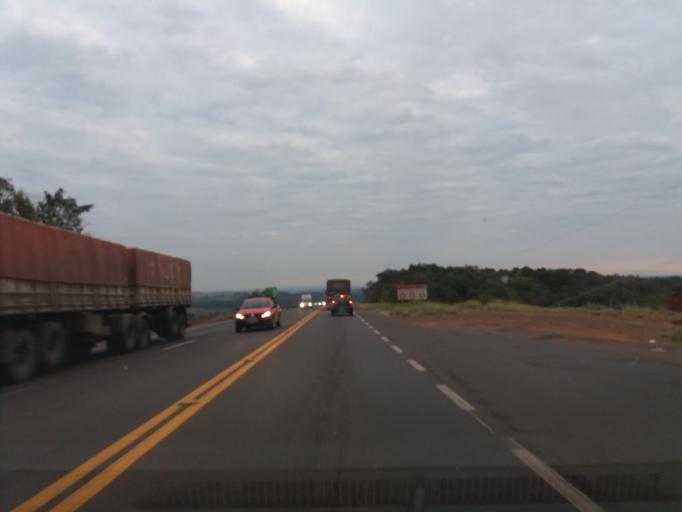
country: BR
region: Parana
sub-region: Cascavel
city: Cascavel
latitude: -25.1936
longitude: -53.6022
